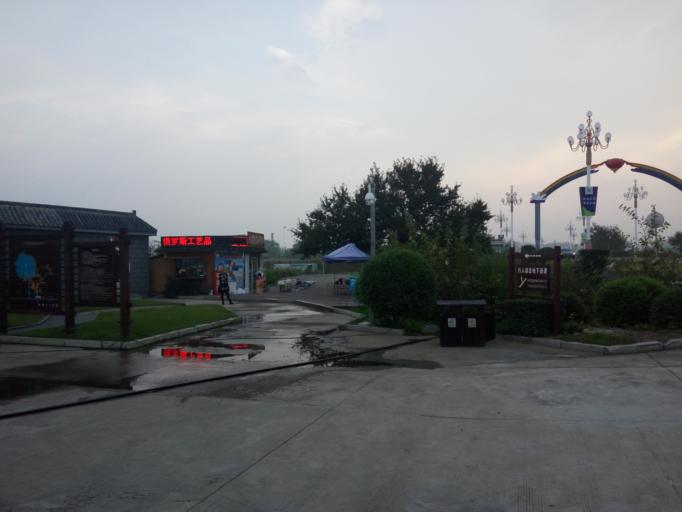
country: CN
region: Heilongjiang Sheng
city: Erjing
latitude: 48.6497
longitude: 126.1490
